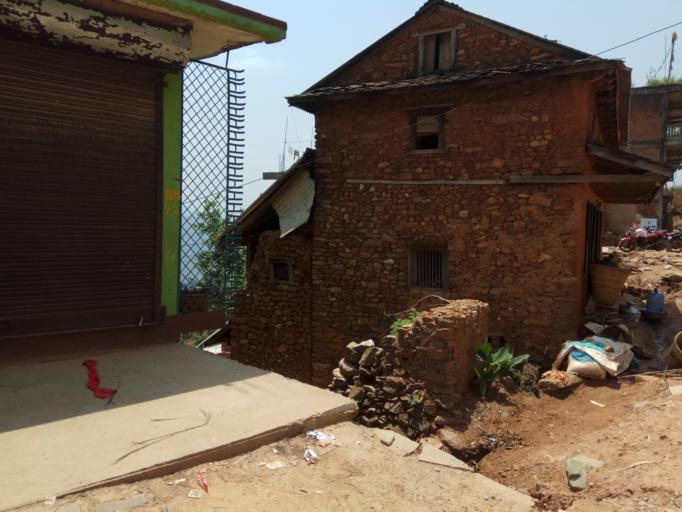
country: NP
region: Central Region
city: Kirtipur
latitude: 27.8959
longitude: 85.0656
